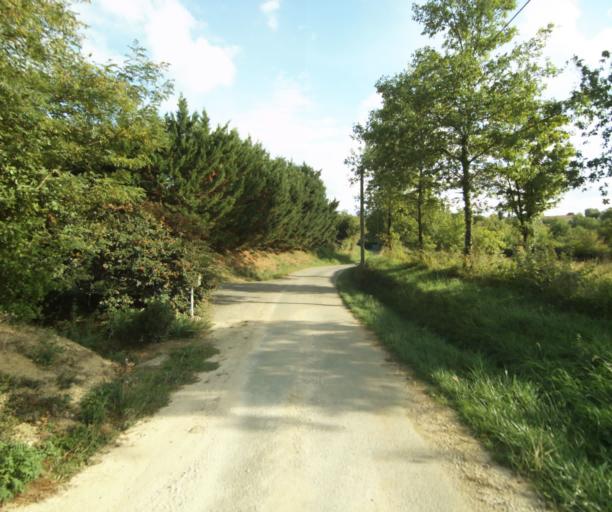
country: FR
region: Midi-Pyrenees
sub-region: Departement du Gers
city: Gondrin
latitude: 43.8922
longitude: 0.2348
